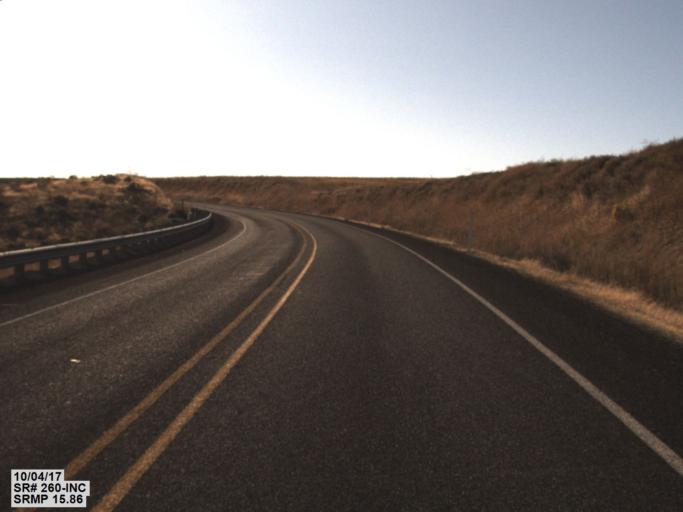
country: US
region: Washington
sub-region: Franklin County
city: Connell
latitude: 46.6254
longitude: -118.7218
